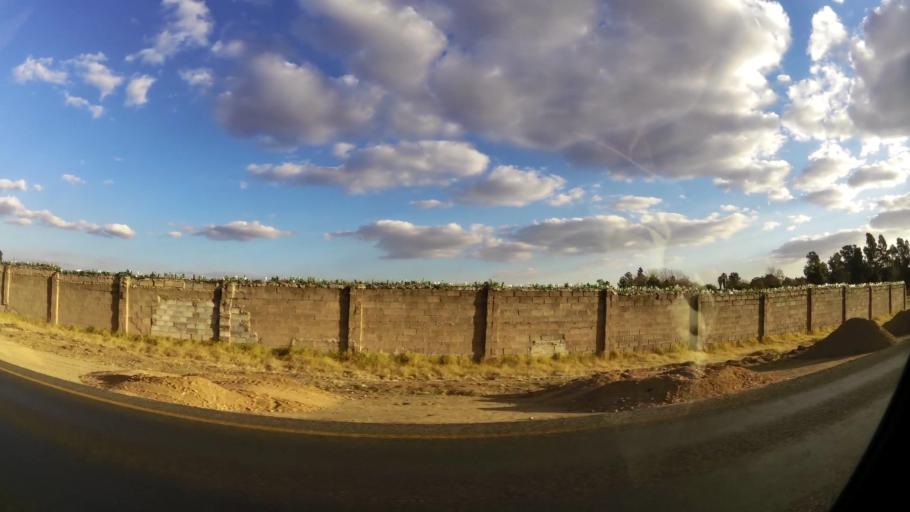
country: ZA
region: Gauteng
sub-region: City of Johannesburg Metropolitan Municipality
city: Midrand
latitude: -25.9478
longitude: 28.1754
